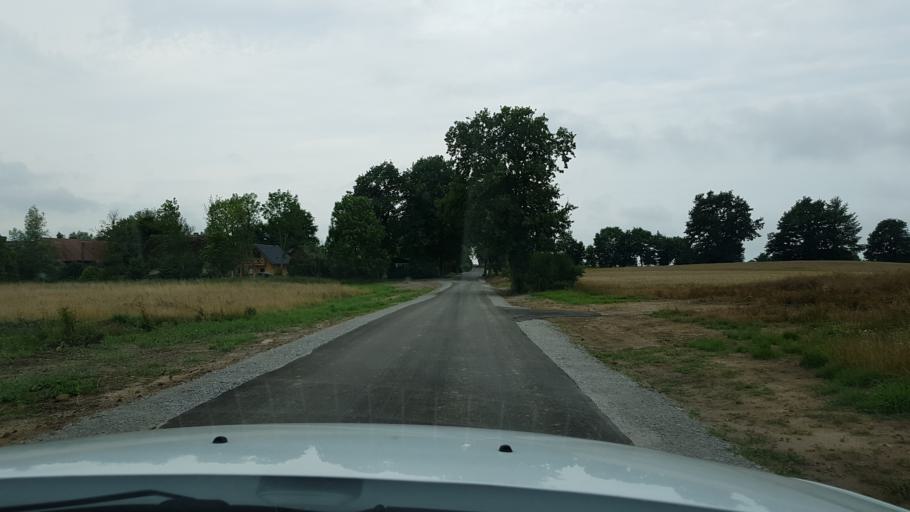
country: PL
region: West Pomeranian Voivodeship
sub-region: Powiat slawienski
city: Darlowo
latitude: 54.4601
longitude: 16.4882
